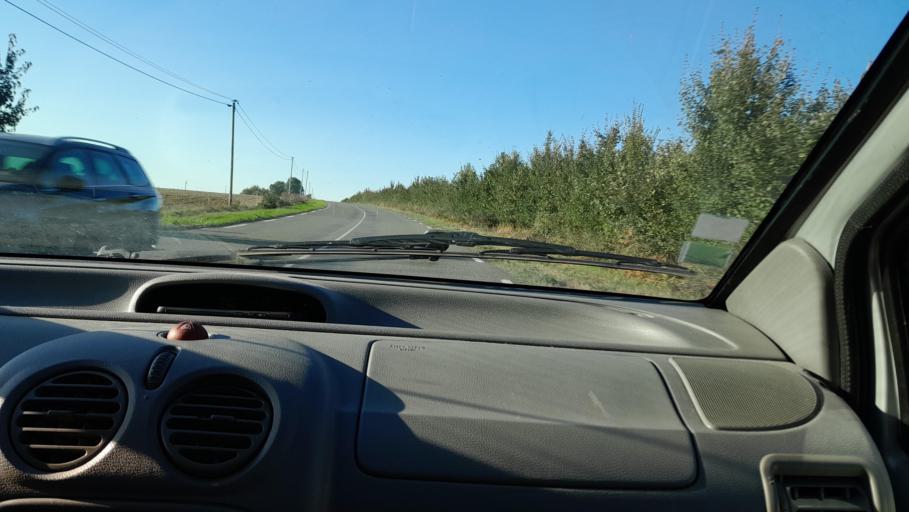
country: FR
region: Pays de la Loire
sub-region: Departement de la Mayenne
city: Ballots
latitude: 47.9032
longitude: -1.0526
